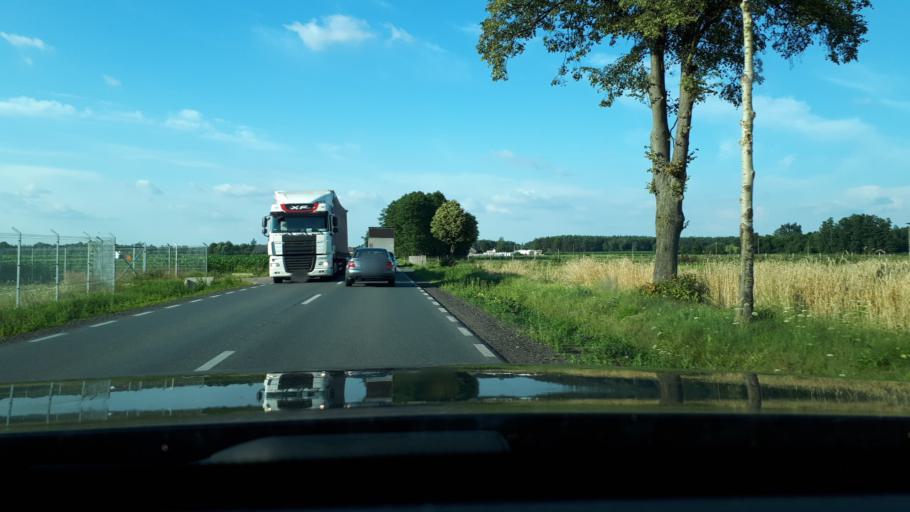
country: PL
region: Masovian Voivodeship
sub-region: Powiat ciechanowski
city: Ojrzen
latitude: 52.7292
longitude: 20.5129
